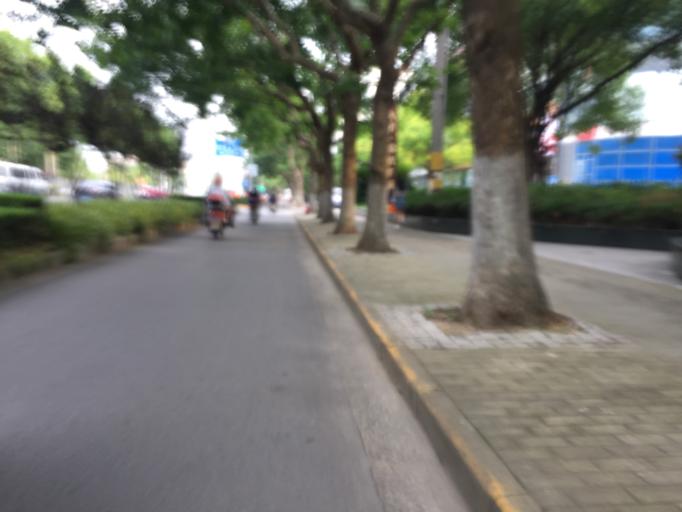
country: CN
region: Shanghai Shi
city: Huamu
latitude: 31.1832
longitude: 121.5372
